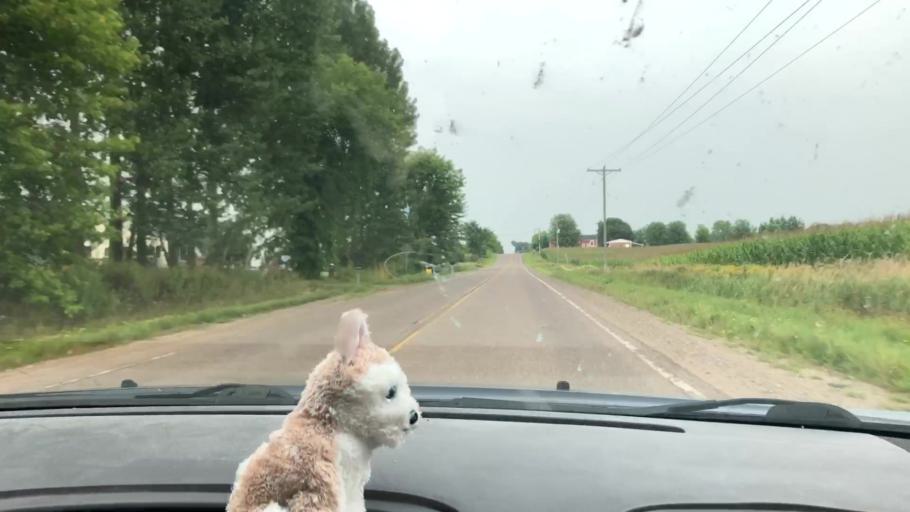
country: US
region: Wisconsin
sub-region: Chippewa County
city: Stanley
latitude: 44.9596
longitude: -90.8815
